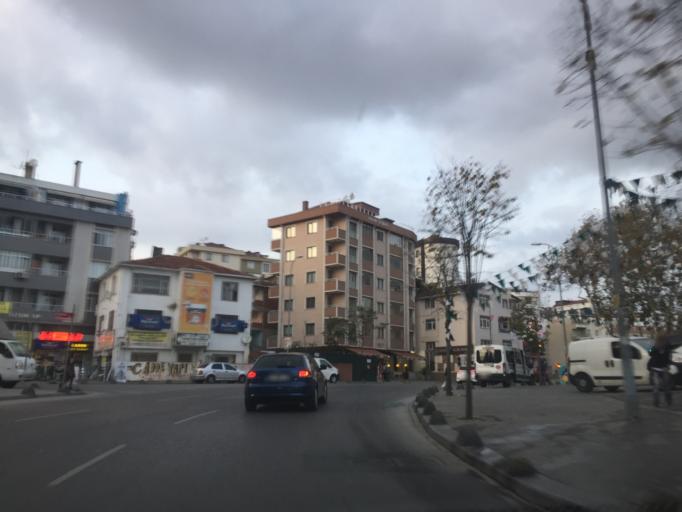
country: TR
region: Istanbul
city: Samandira
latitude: 40.9865
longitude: 29.2322
